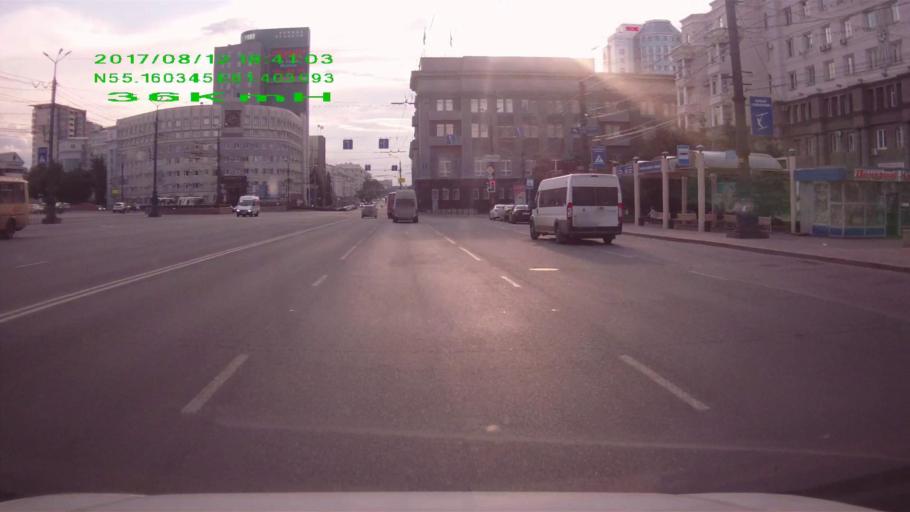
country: RU
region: Chelyabinsk
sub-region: Gorod Chelyabinsk
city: Chelyabinsk
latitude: 55.1584
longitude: 61.3982
